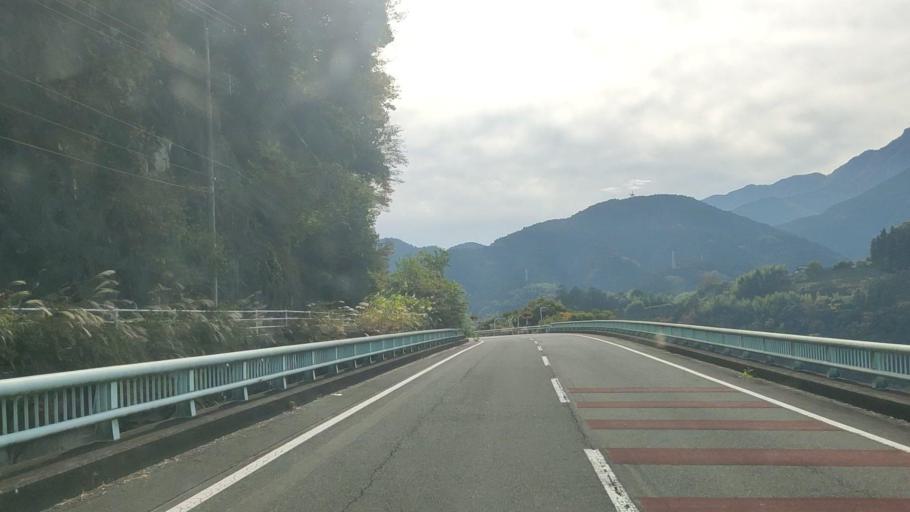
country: JP
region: Shizuoka
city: Fujinomiya
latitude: 35.2702
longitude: 138.4710
